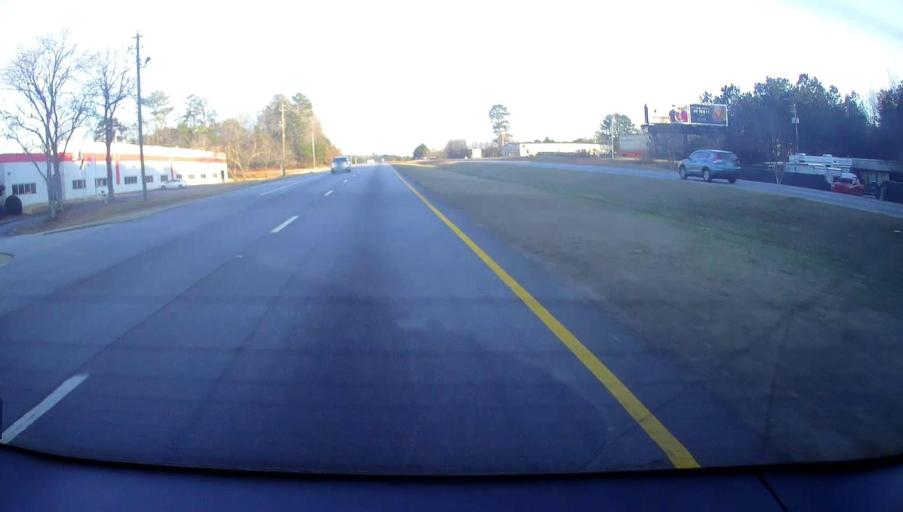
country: US
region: Georgia
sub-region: Fulton County
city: Fairburn
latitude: 33.5542
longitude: -84.5860
